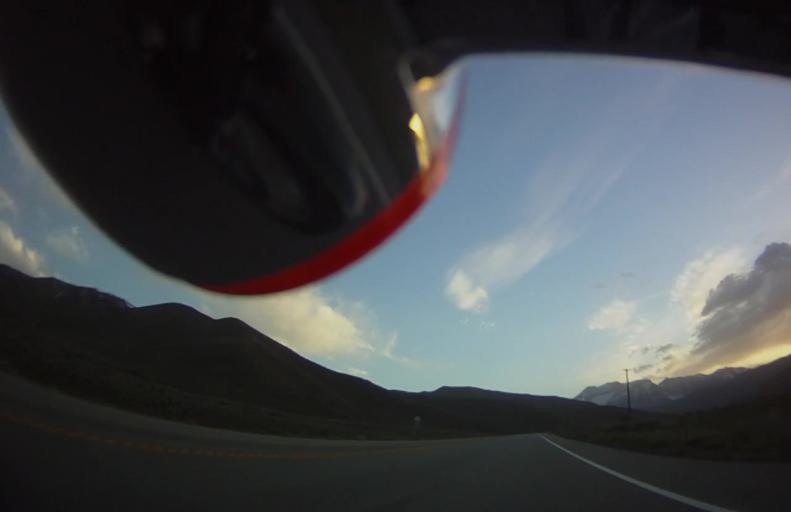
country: US
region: Utah
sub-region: Wasatch County
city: Midway
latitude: 40.4090
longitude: -111.4803
